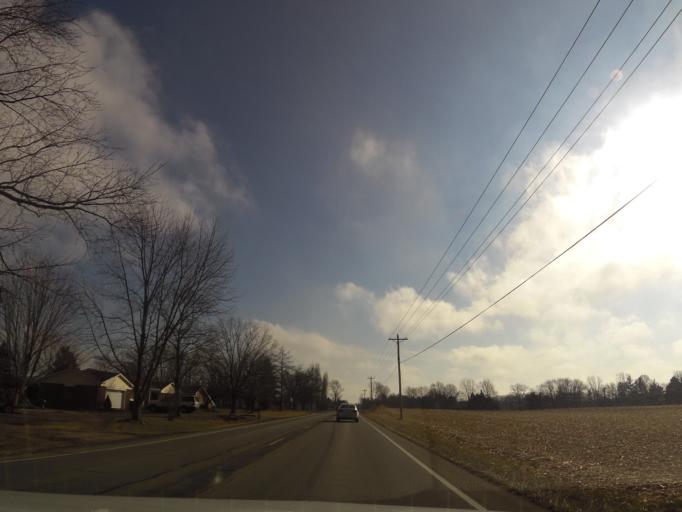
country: US
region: Indiana
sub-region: Jennings County
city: Country Squire Lakes
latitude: 39.1313
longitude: -85.7782
